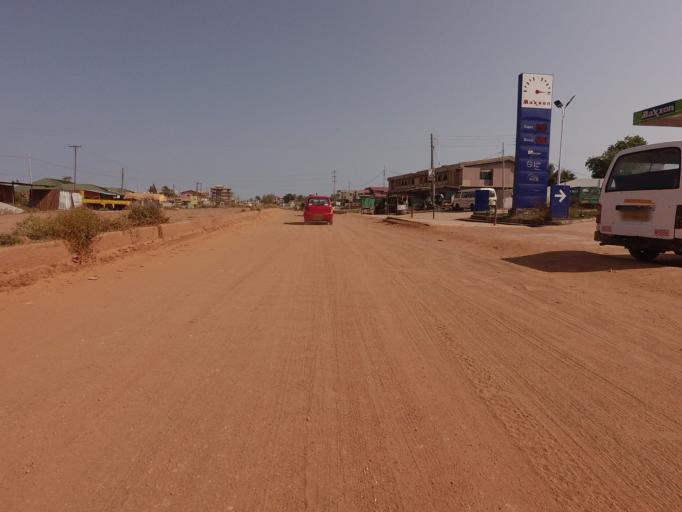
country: GH
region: Greater Accra
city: Teshi Old Town
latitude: 5.6169
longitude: -0.1248
